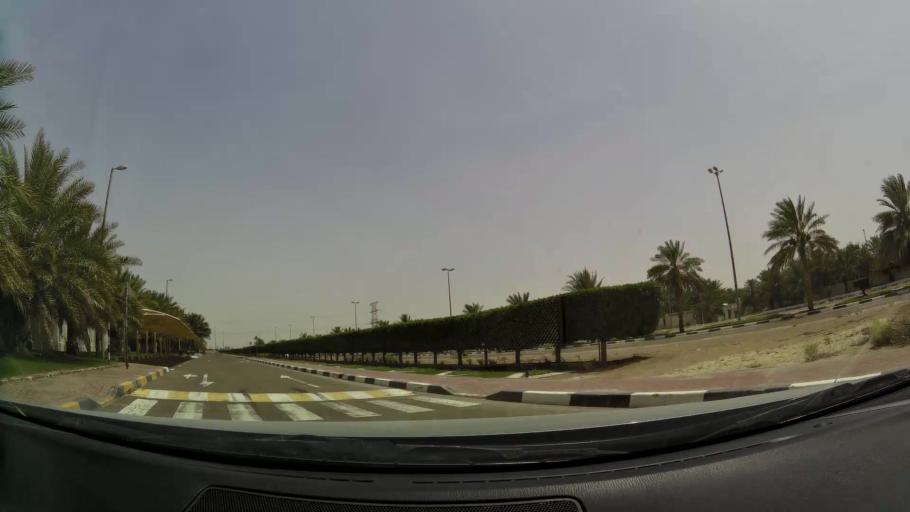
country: AE
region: Abu Dhabi
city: Al Ain
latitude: 24.1873
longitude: 55.6785
